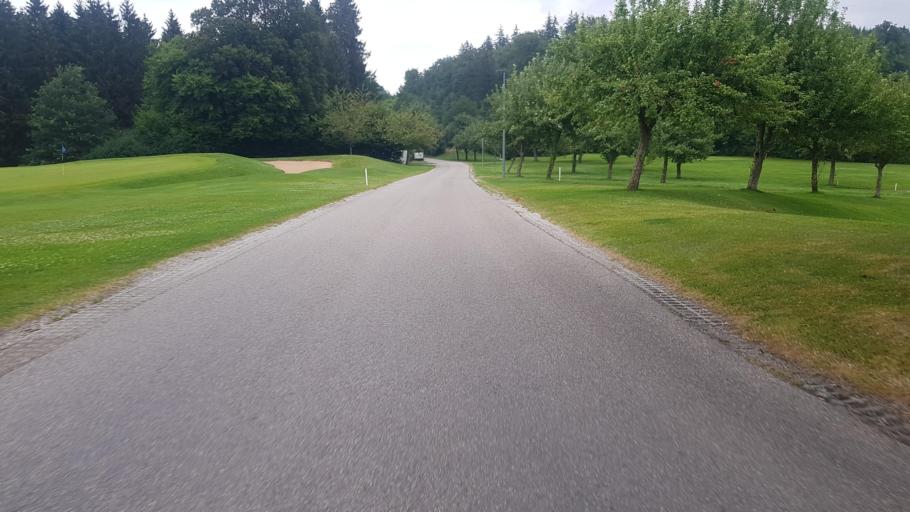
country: DE
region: Bavaria
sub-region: Upper Bavaria
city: Starnberg
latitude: 48.0259
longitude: 11.3486
